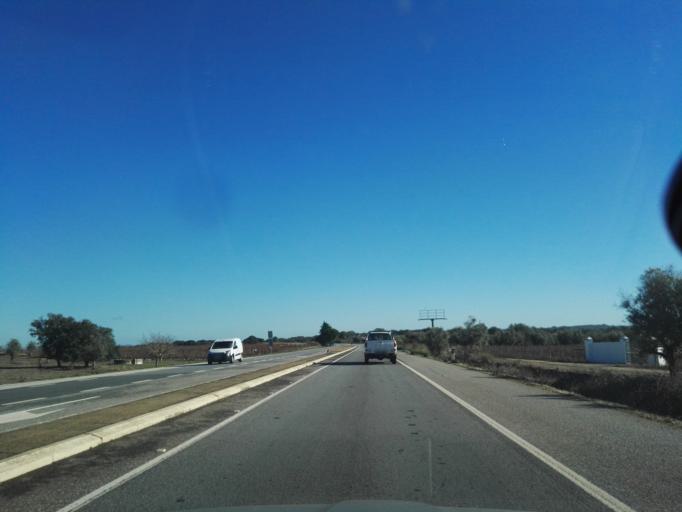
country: PT
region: Evora
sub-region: Estremoz
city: Estremoz
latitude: 38.8259
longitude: -7.5218
